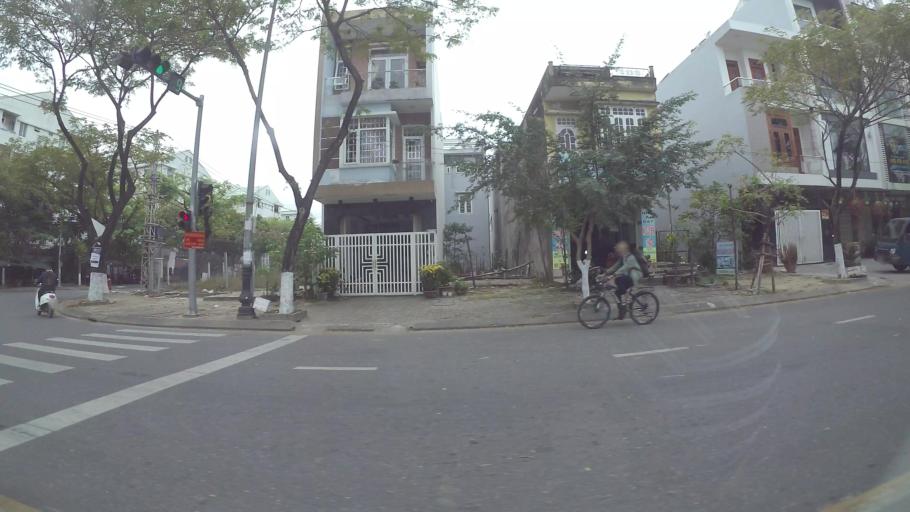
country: VN
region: Da Nang
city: Lien Chieu
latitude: 16.0757
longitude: 108.1679
